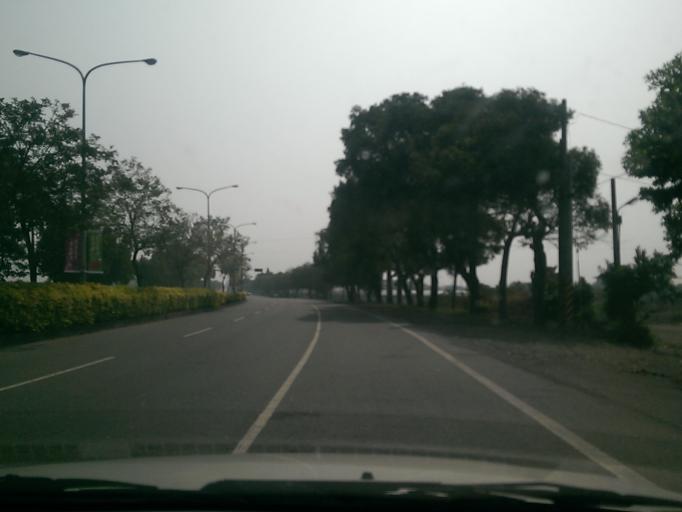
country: TW
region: Taiwan
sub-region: Yunlin
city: Douliu
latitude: 23.7719
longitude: 120.4807
